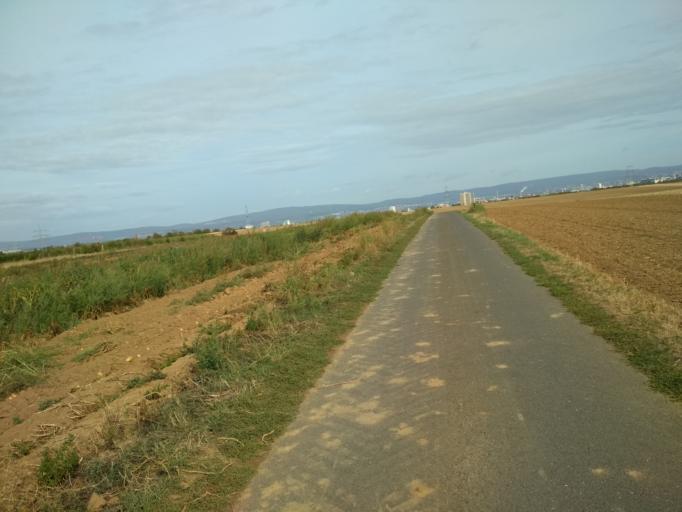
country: DE
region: Rheinland-Pfalz
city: Klein-Winternheim
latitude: 49.9564
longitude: 8.2481
